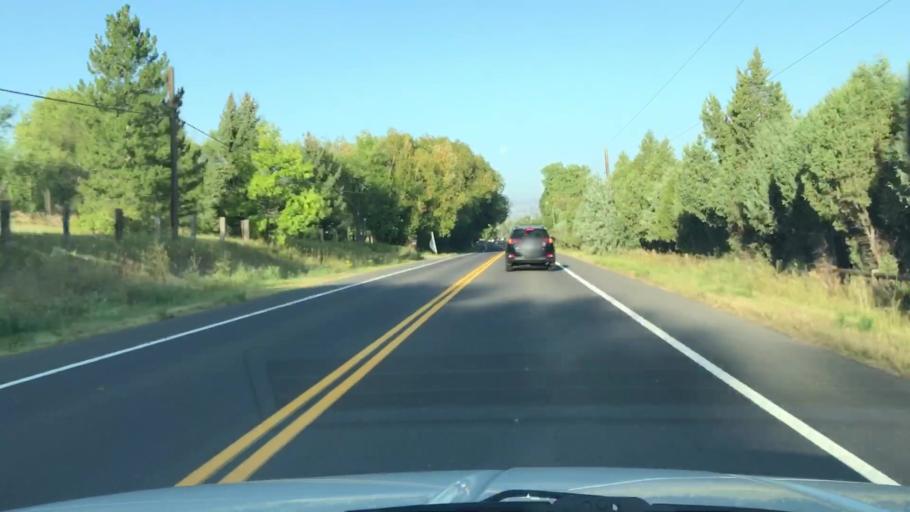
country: US
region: Colorado
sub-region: Boulder County
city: Gunbarrel
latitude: 40.0340
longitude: -105.1746
